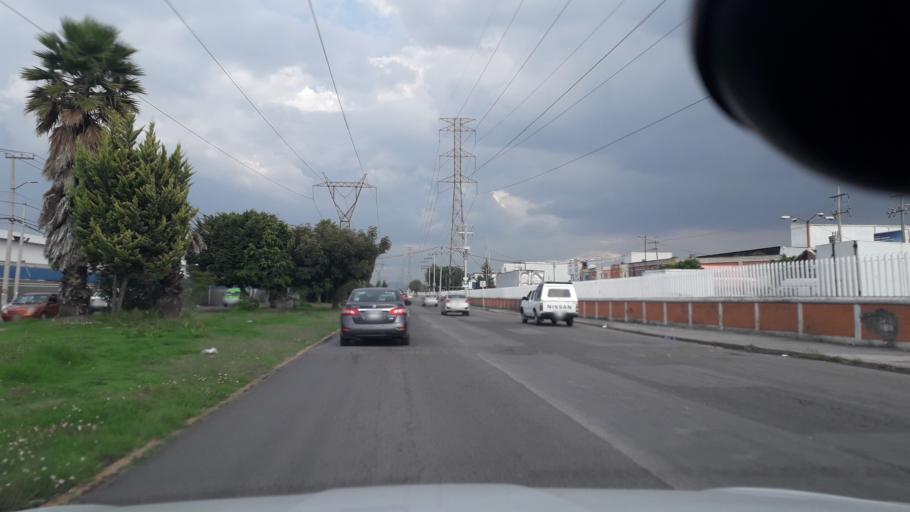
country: MX
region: Mexico
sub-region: Tultitlan
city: Fuentes del Valle
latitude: 19.6401
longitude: -99.1408
